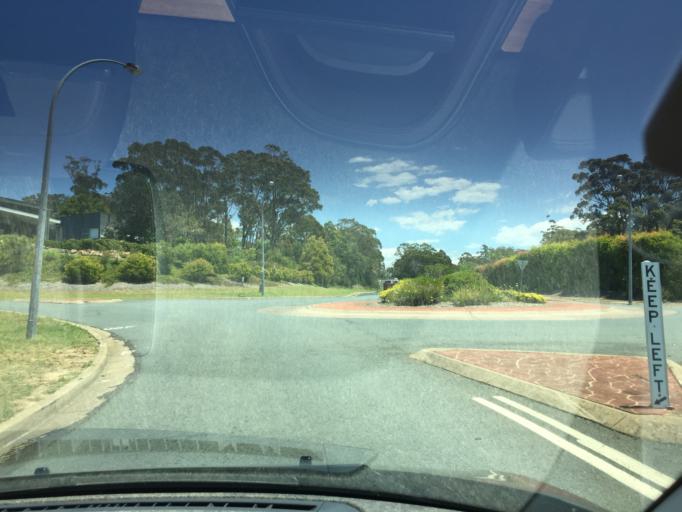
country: AU
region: New South Wales
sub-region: Bega Valley
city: Merimbula
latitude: -36.8487
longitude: 149.9276
